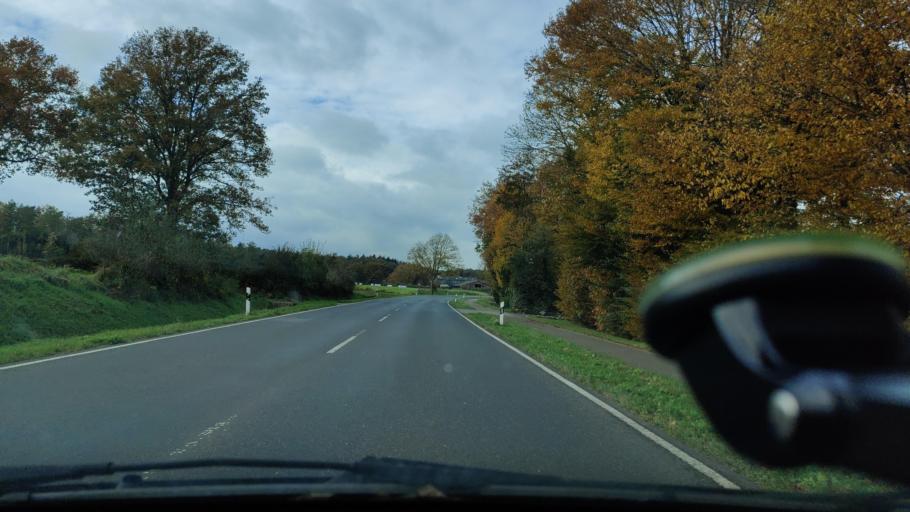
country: DE
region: North Rhine-Westphalia
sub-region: Regierungsbezirk Dusseldorf
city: Sonsbeck
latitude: 51.6365
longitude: 6.3983
